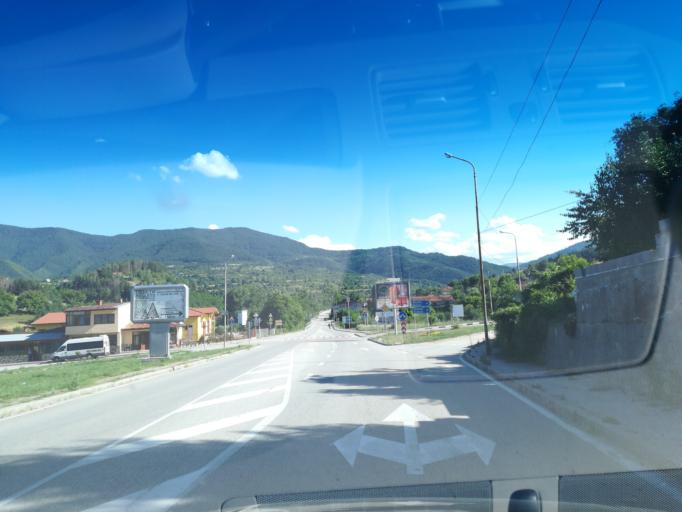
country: BG
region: Plovdiv
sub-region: Obshtina Luki
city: Luki
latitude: 41.8714
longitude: 24.6911
